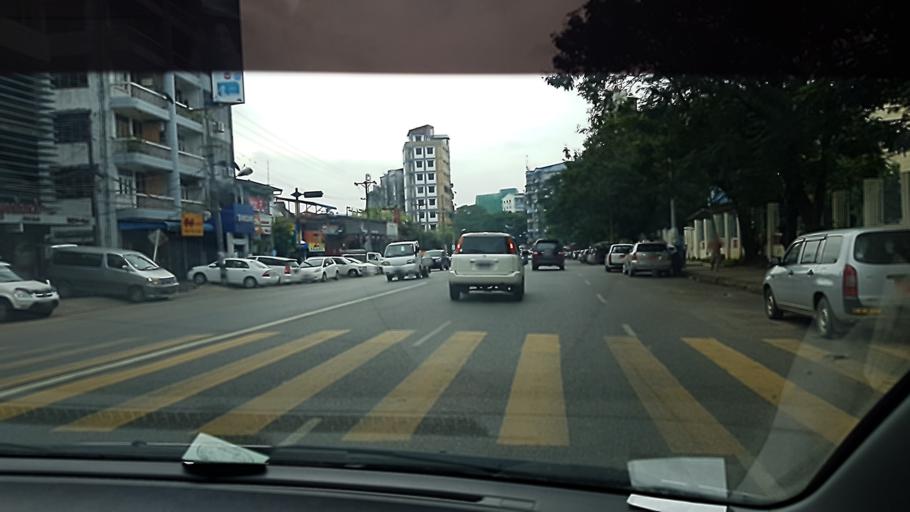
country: MM
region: Yangon
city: Yangon
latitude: 16.7961
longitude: 96.1261
